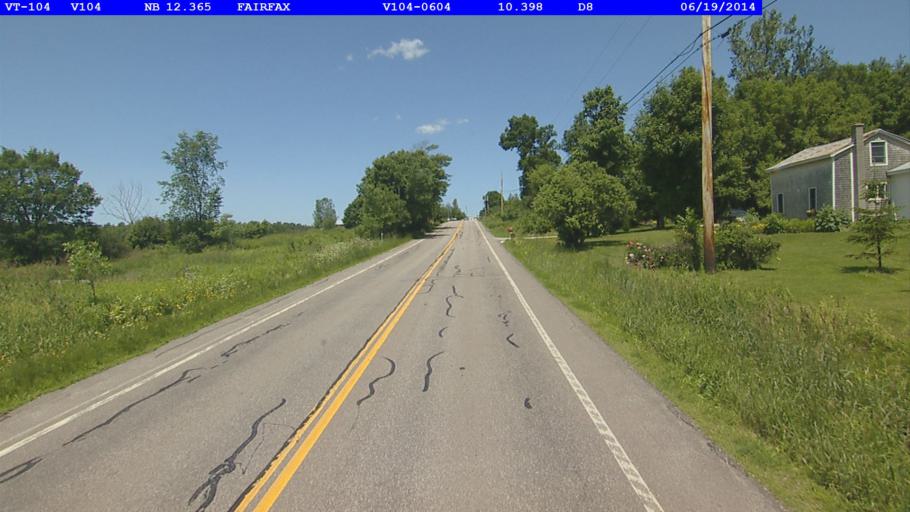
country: US
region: Vermont
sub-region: Franklin County
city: Saint Albans
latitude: 44.7338
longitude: -73.0477
